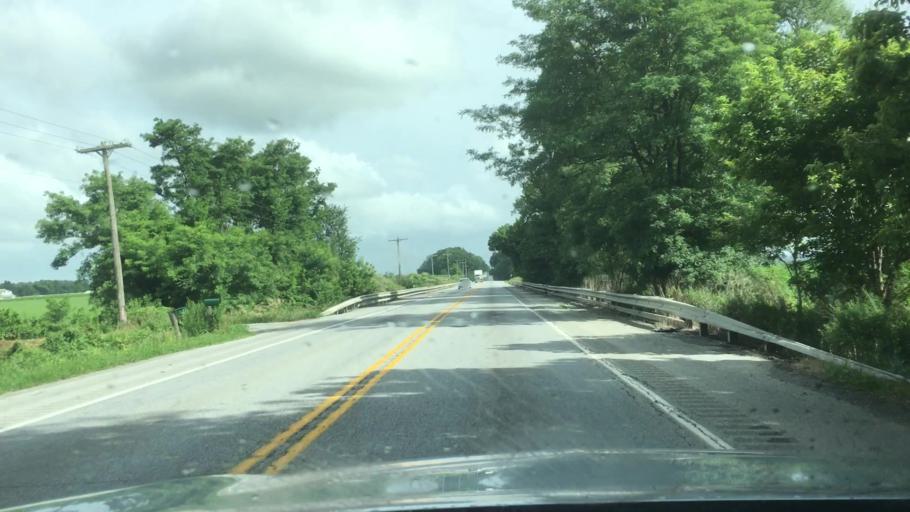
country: US
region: Pennsylvania
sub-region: Chester County
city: Atglen
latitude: 39.9241
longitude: -75.9459
